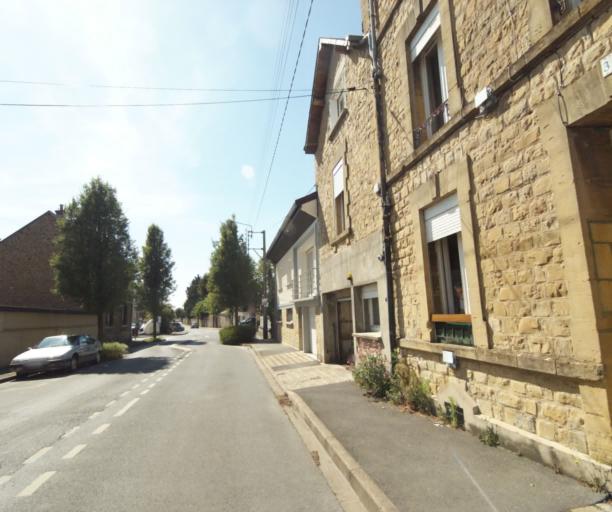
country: FR
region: Champagne-Ardenne
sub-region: Departement des Ardennes
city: Charleville-Mezieres
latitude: 49.7606
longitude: 4.7102
